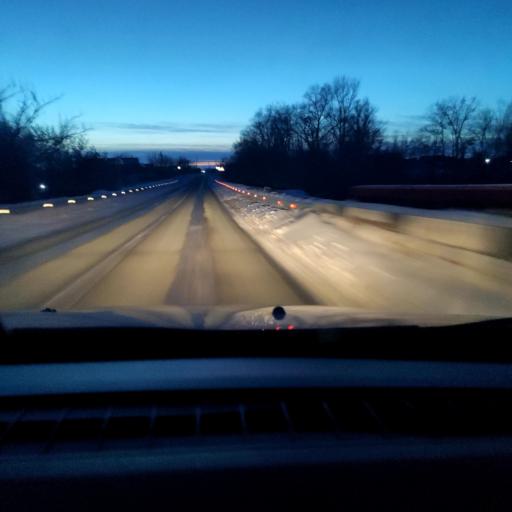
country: RU
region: Samara
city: Kinel'
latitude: 53.2981
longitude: 50.7692
